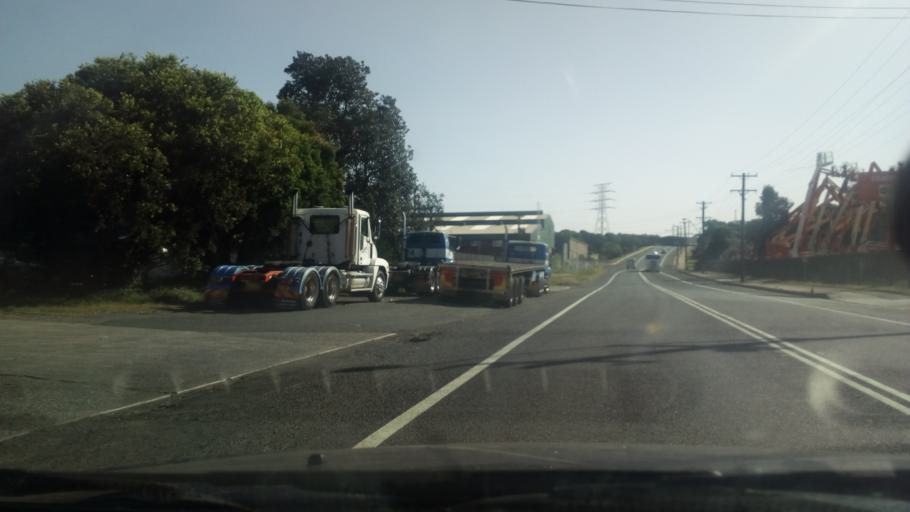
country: AU
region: New South Wales
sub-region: Wollongong
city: Cringila
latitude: -34.4709
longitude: 150.8924
